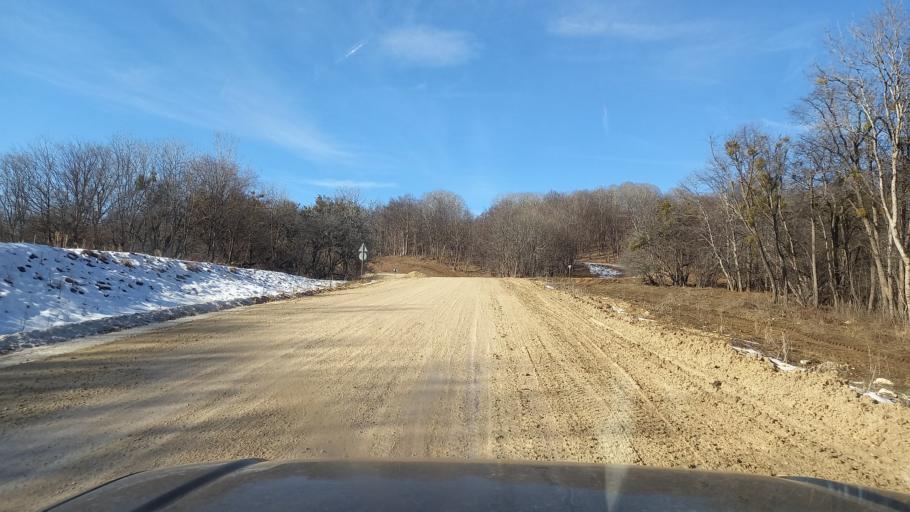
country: RU
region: Adygeya
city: Kamennomostskiy
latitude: 44.2817
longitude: 40.3221
